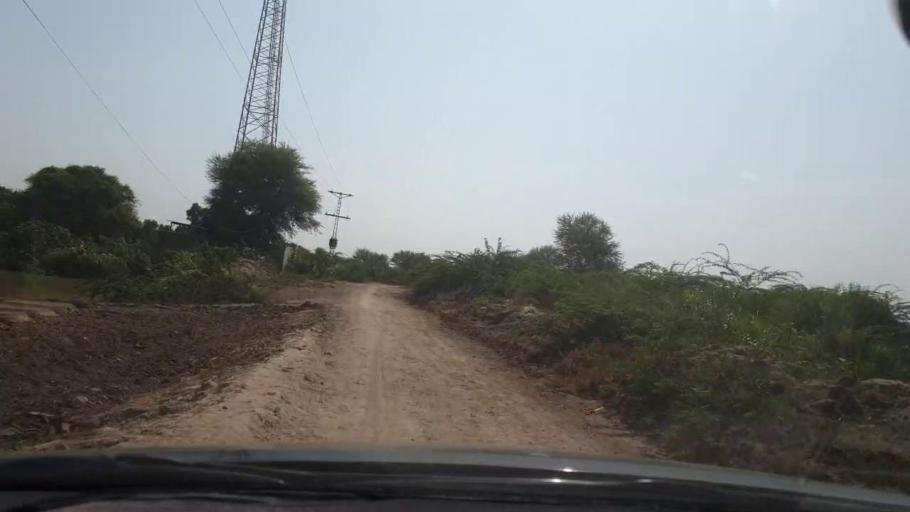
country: PK
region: Sindh
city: Naukot
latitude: 24.8105
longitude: 69.2618
